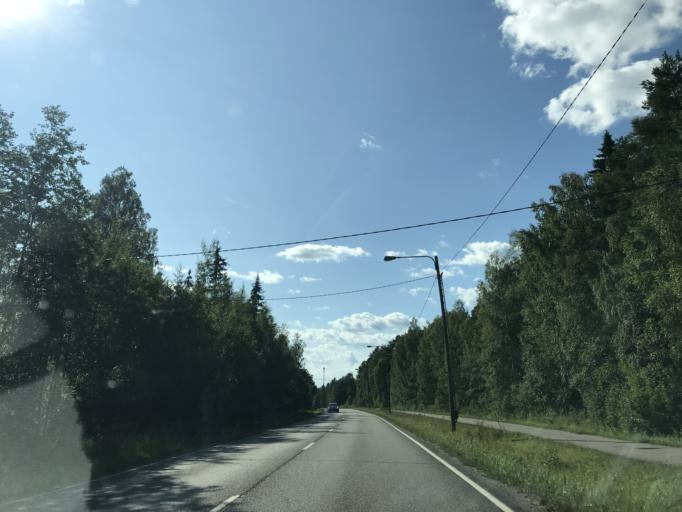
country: FI
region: Uusimaa
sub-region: Helsinki
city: Tuusula
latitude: 60.4063
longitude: 24.9630
